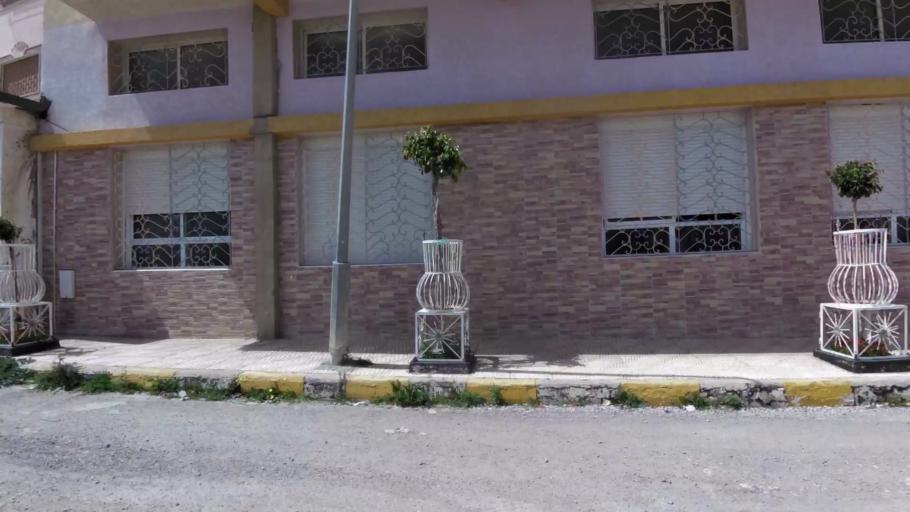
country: MA
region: Tanger-Tetouan
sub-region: Tanger-Assilah
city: Tangier
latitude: 35.7480
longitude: -5.8449
